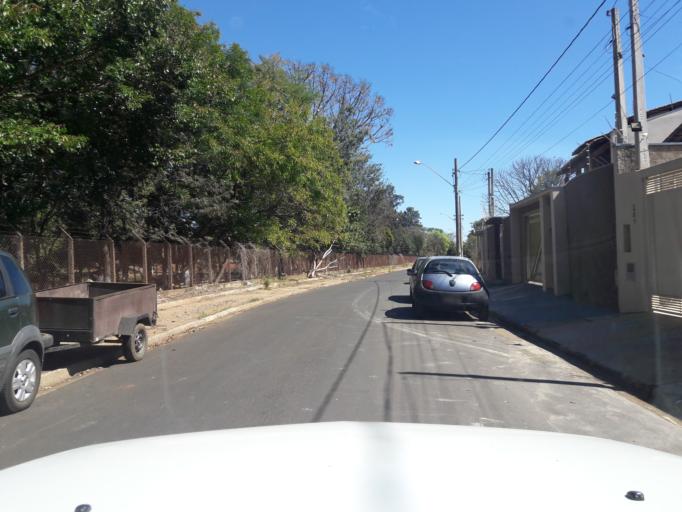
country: BR
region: Sao Paulo
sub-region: Moji-Guacu
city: Mogi-Gaucu
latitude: -22.3410
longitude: -46.9316
